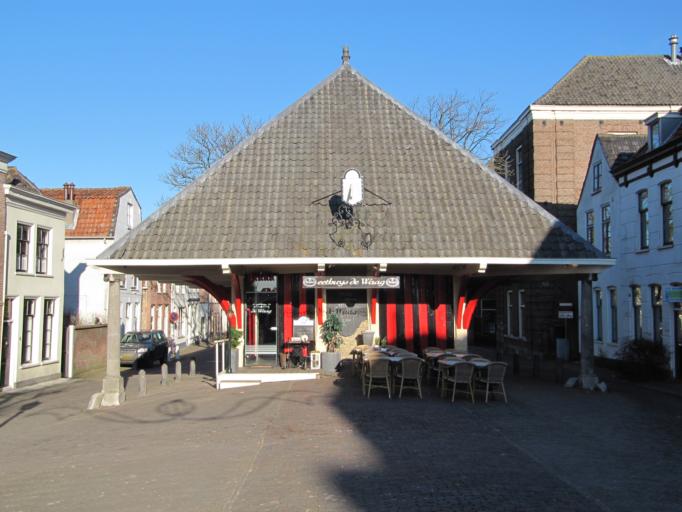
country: NL
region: South Holland
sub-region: Gemeente Schoonhoven
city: Schoonhoven
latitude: 51.9467
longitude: 4.8516
